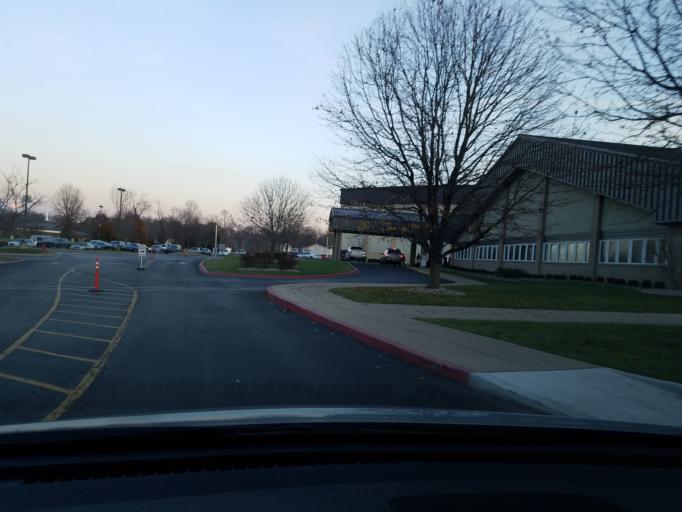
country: US
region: Indiana
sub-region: Clark County
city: Sellersburg
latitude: 38.3545
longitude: -85.7954
